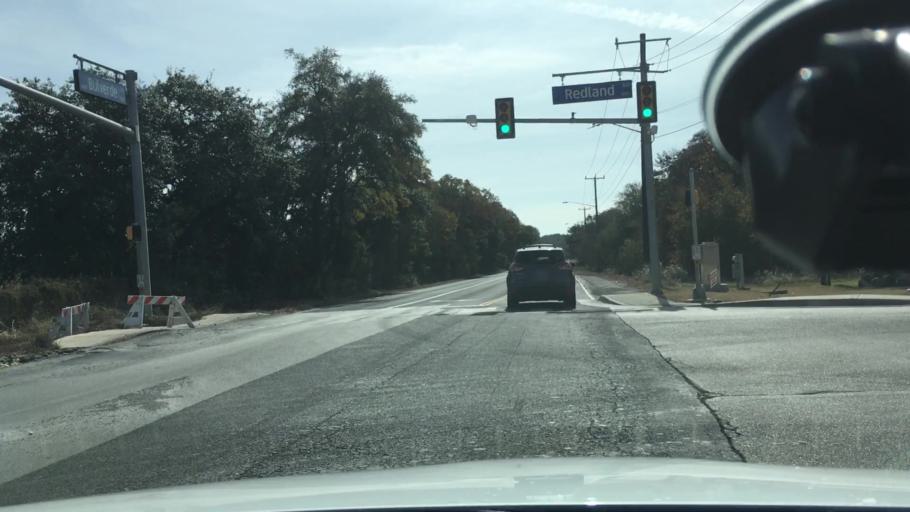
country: US
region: Texas
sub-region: Bexar County
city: Hollywood Park
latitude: 29.5931
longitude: -98.4244
